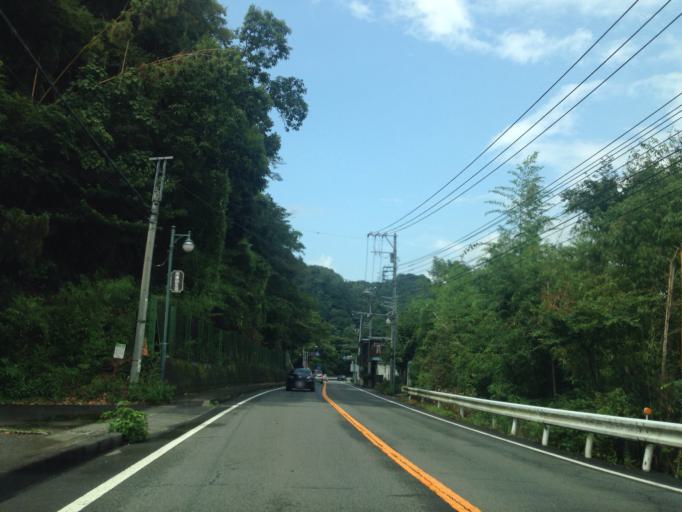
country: JP
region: Shizuoka
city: Heda
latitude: 34.9389
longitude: 138.9311
